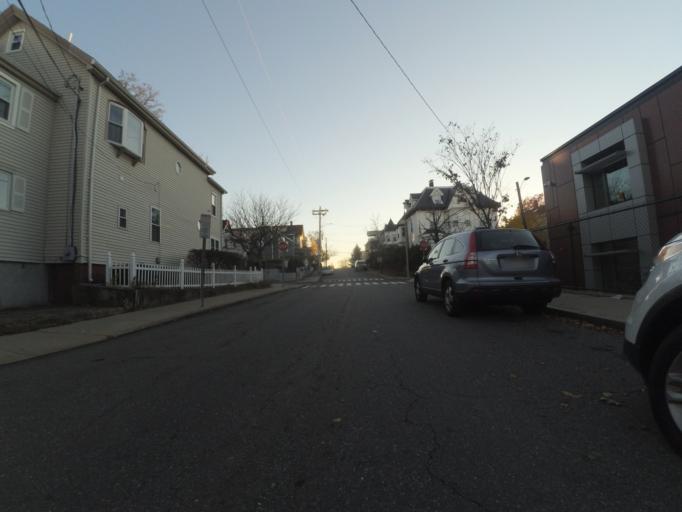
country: US
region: Massachusetts
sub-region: Middlesex County
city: Somerville
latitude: 42.3854
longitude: -71.0859
